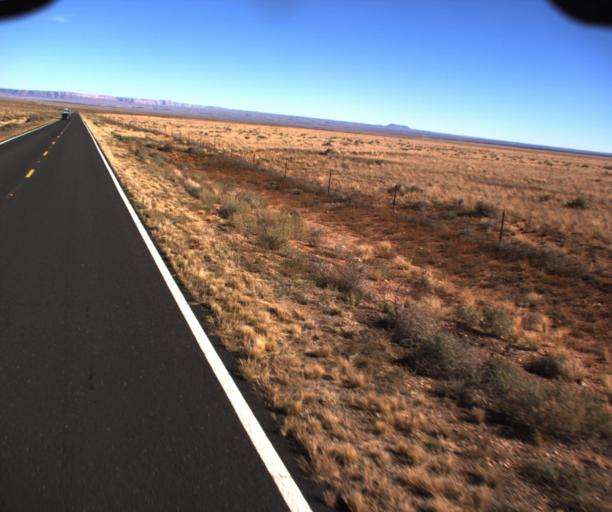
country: US
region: Arizona
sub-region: Coconino County
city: Fredonia
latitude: 36.7214
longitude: -112.0141
